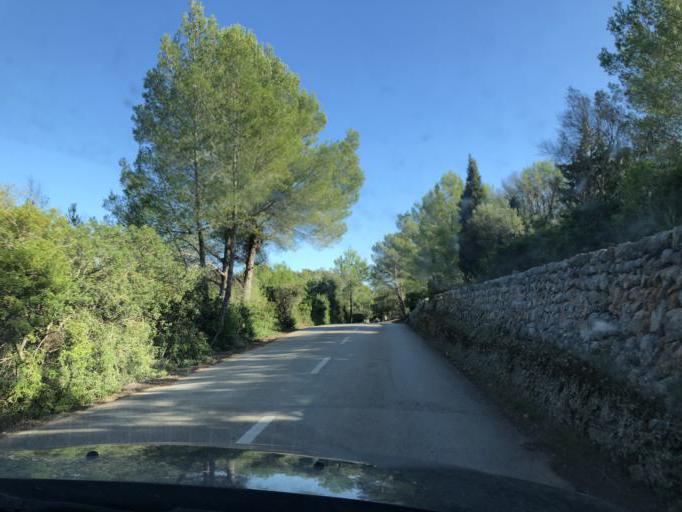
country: ES
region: Balearic Islands
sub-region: Illes Balears
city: Camp de Mar
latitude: 39.5401
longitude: 2.4034
